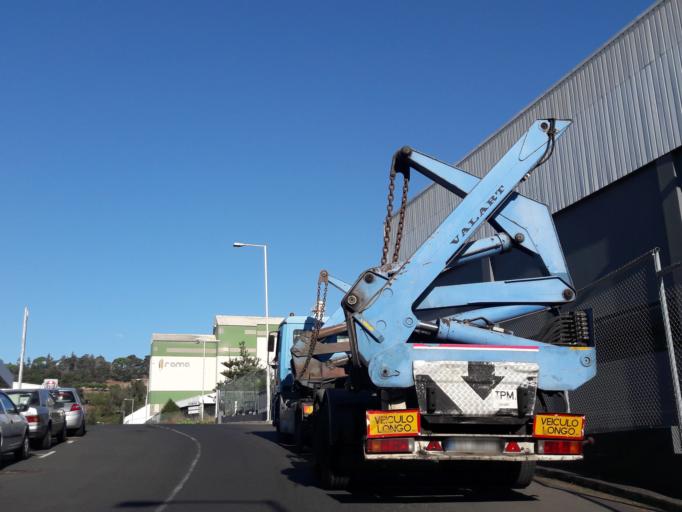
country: PT
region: Madeira
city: Canico
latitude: 32.6517
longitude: -16.8595
